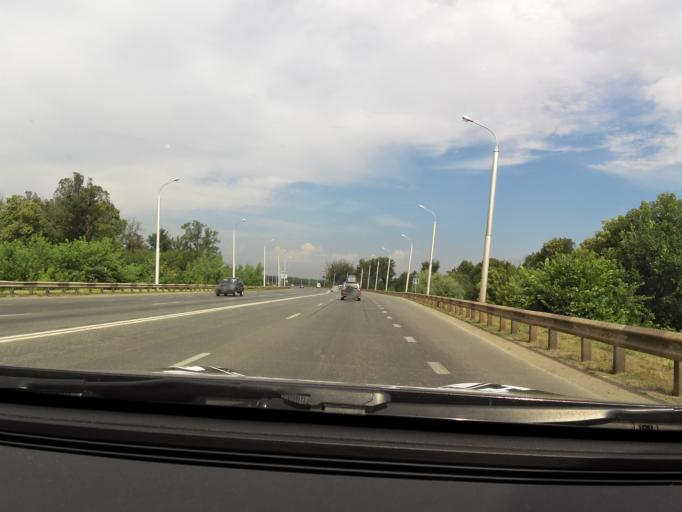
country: RU
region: Bashkortostan
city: Iglino
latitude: 54.7966
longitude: 56.2065
